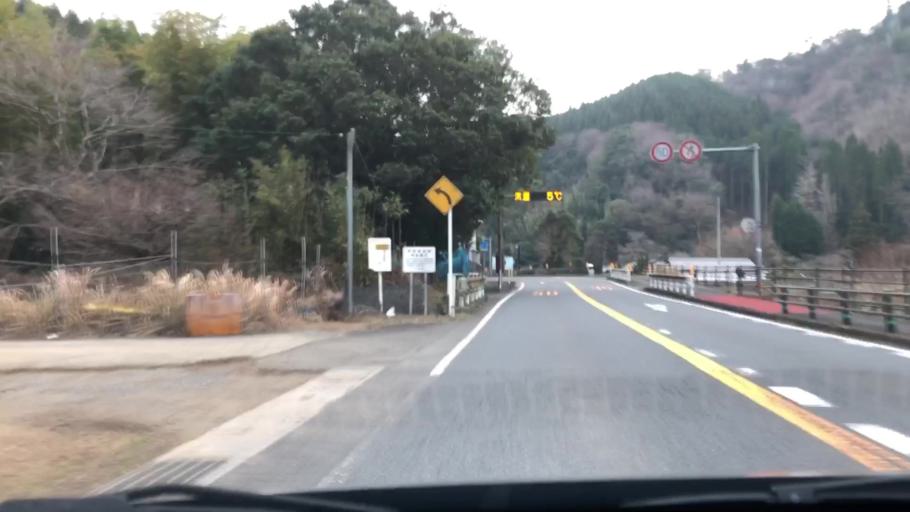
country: JP
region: Oita
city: Usuki
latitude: 32.9963
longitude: 131.7586
